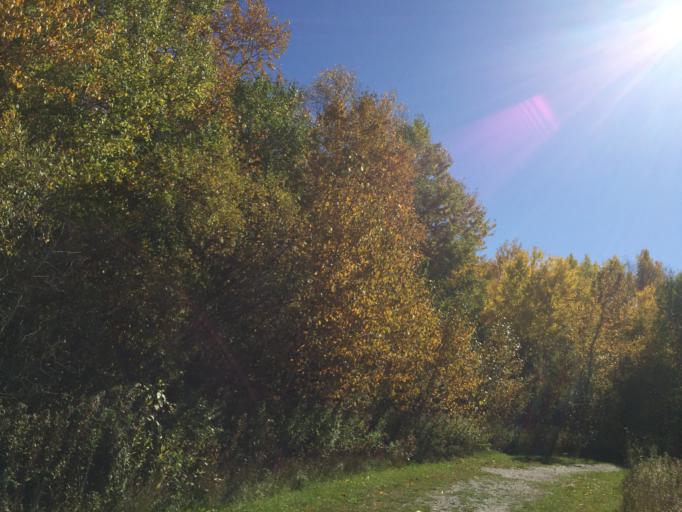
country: US
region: Minnesota
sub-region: Lake of the Woods County
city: Baudette
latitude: 48.2865
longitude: -94.5658
